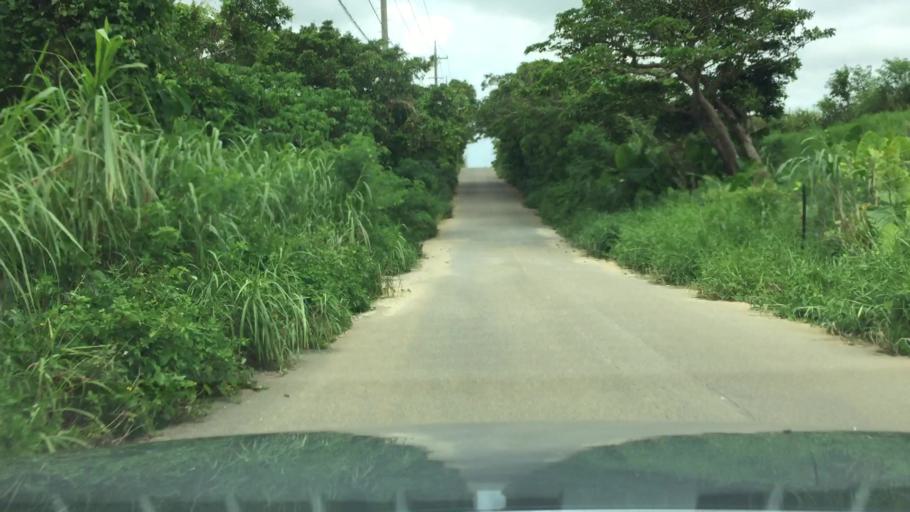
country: JP
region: Okinawa
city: Ishigaki
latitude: 24.3950
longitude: 124.1754
